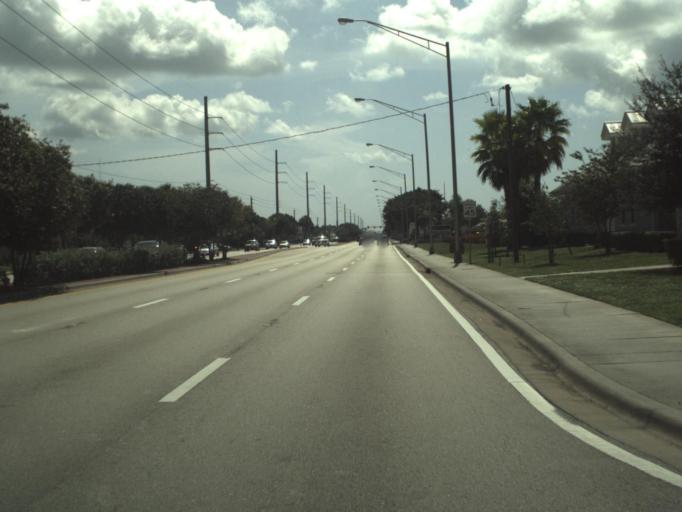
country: US
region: Florida
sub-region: Saint Lucie County
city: Port Saint Lucie
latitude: 27.2710
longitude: -80.3027
